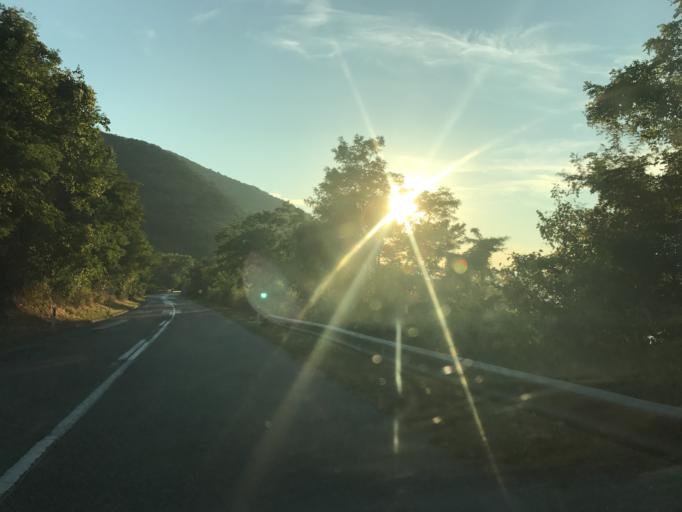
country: RO
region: Caras-Severin
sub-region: Comuna Berzasca
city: Berzasca
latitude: 44.6296
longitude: 21.9627
